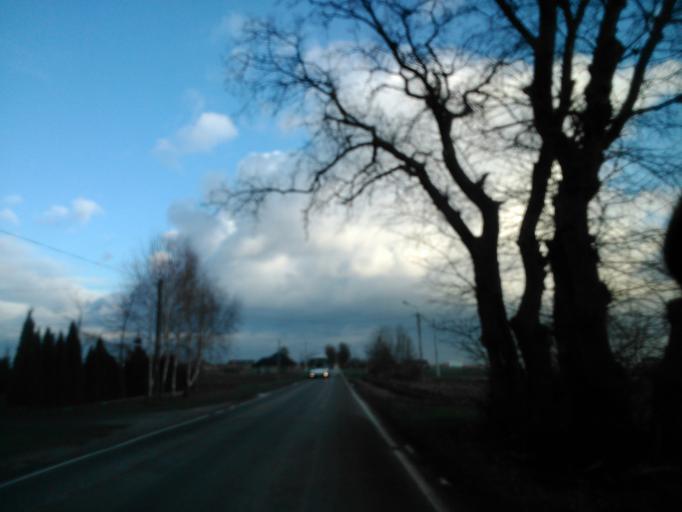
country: PL
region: Masovian Voivodeship
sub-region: Powiat warszawski zachodni
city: Leszno
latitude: 52.2432
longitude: 20.6240
